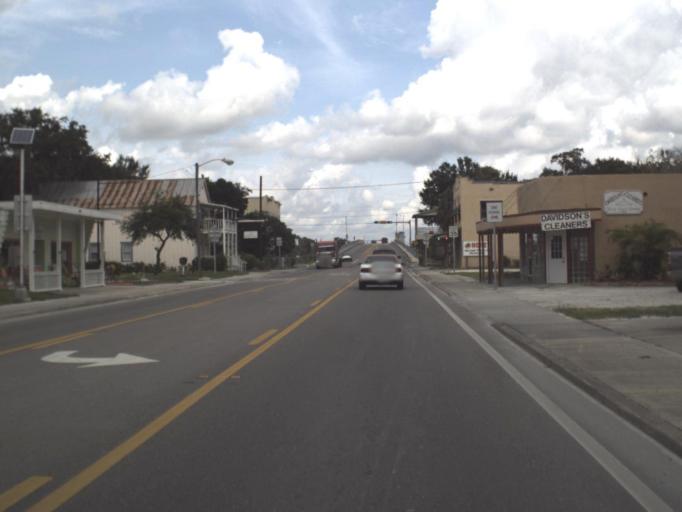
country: US
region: Florida
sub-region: Hendry County
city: LaBelle
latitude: 26.7663
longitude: -81.4374
